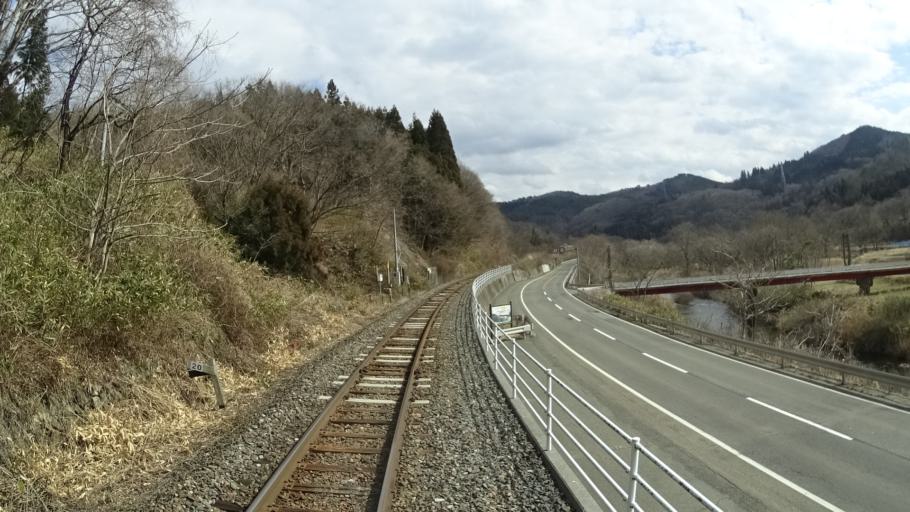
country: JP
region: Iwate
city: Hanamaki
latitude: 39.3595
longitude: 141.3067
